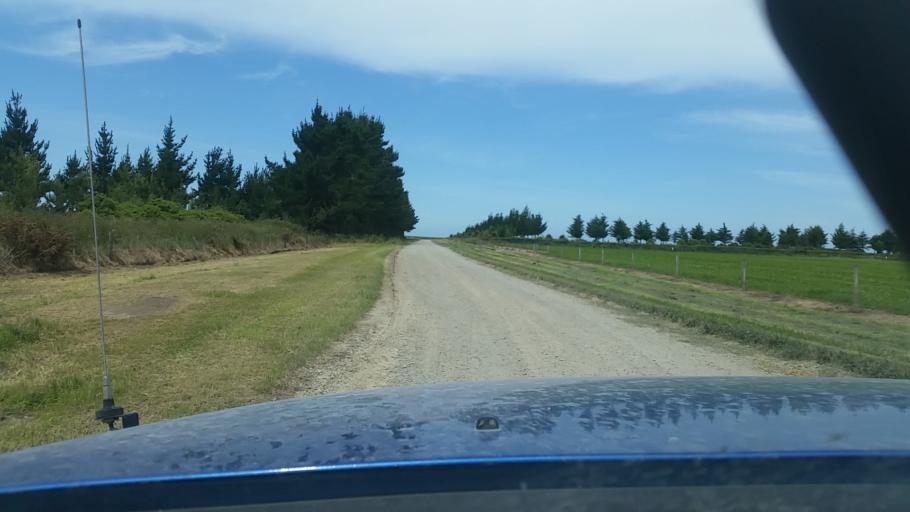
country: NZ
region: Canterbury
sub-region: Ashburton District
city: Tinwald
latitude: -44.0543
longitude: 171.7879
